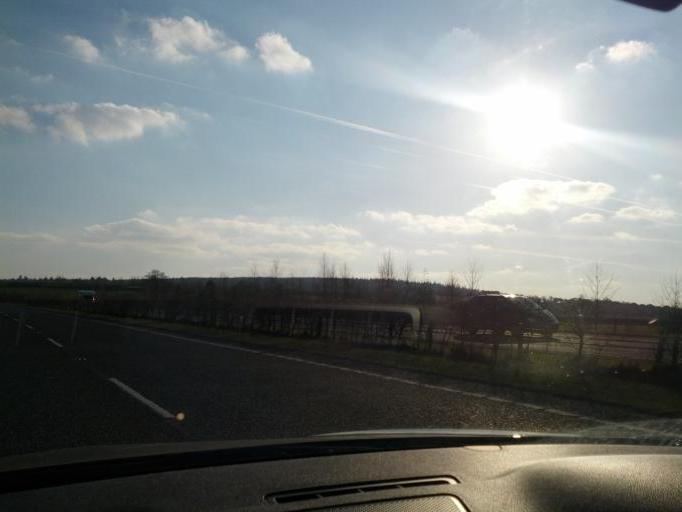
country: IE
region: Leinster
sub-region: Kildare
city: Monasterevin
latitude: 53.1361
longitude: -7.0345
